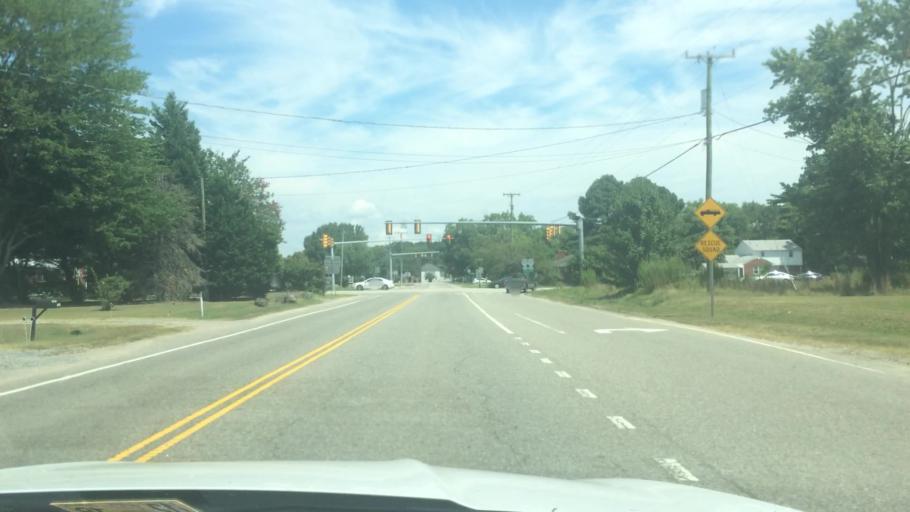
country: US
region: Virginia
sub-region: City of Poquoson
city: Poquoson
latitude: 37.1214
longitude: -76.4323
